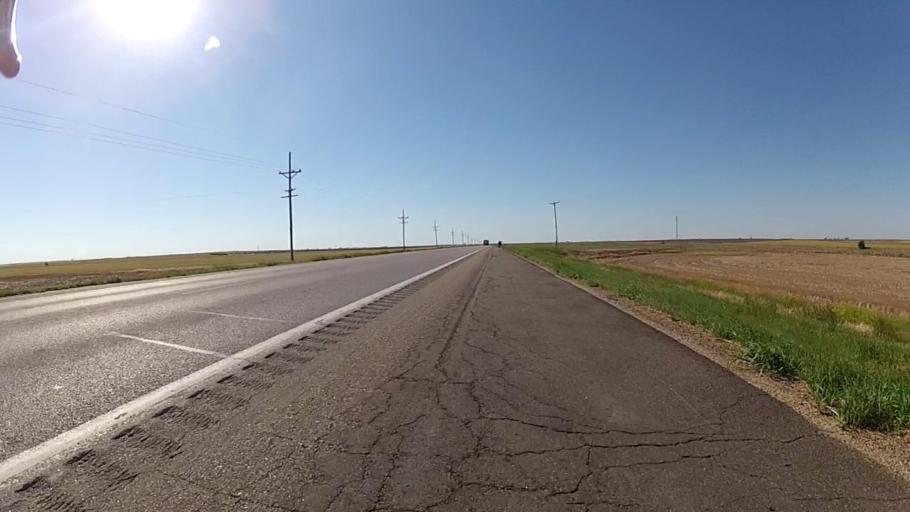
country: US
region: Kansas
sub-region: Ford County
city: Dodge City
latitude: 37.6066
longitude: -99.7089
